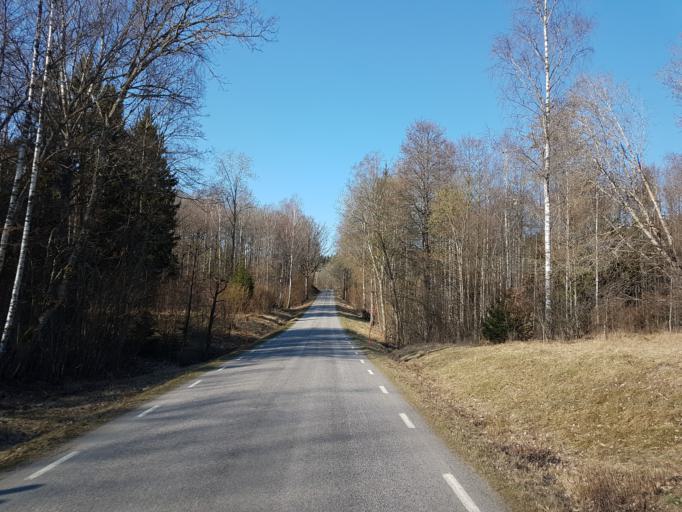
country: SE
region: Kalmar
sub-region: Vasterviks Kommun
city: Overum
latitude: 58.1724
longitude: 16.2710
